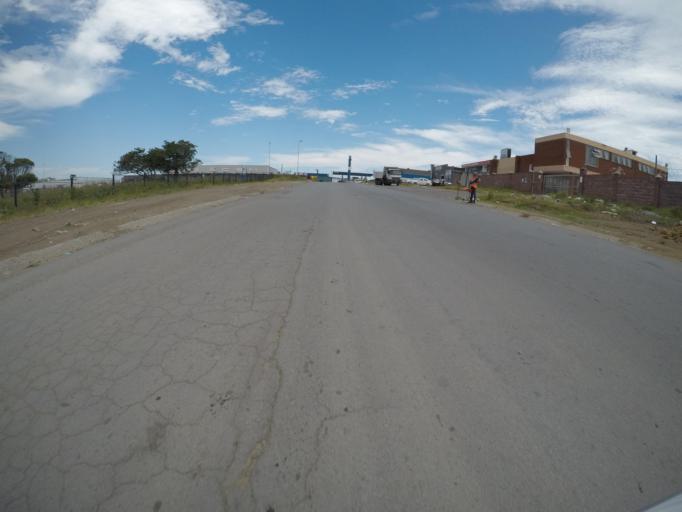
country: ZA
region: Eastern Cape
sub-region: Buffalo City Metropolitan Municipality
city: East London
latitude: -33.0336
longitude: 27.8812
